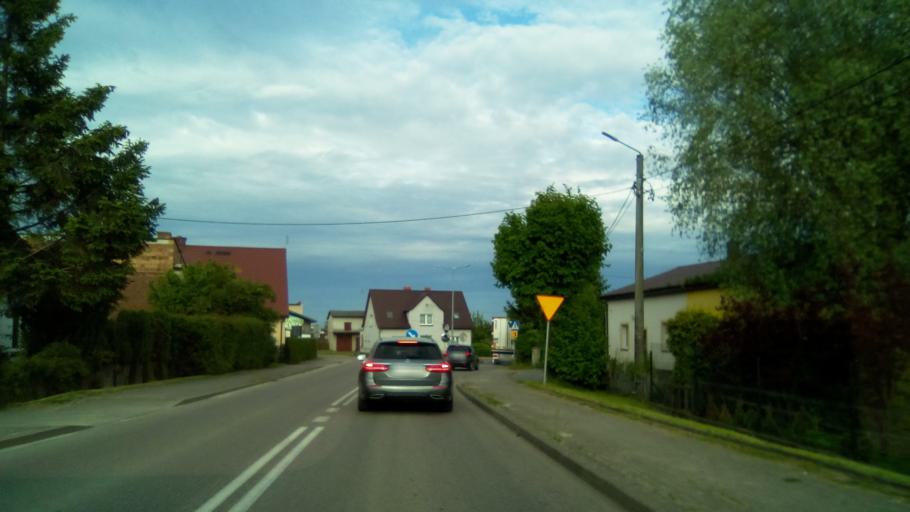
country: PL
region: Pomeranian Voivodeship
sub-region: Powiat pucki
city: Gniezdzewo
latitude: 54.7462
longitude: 18.3779
